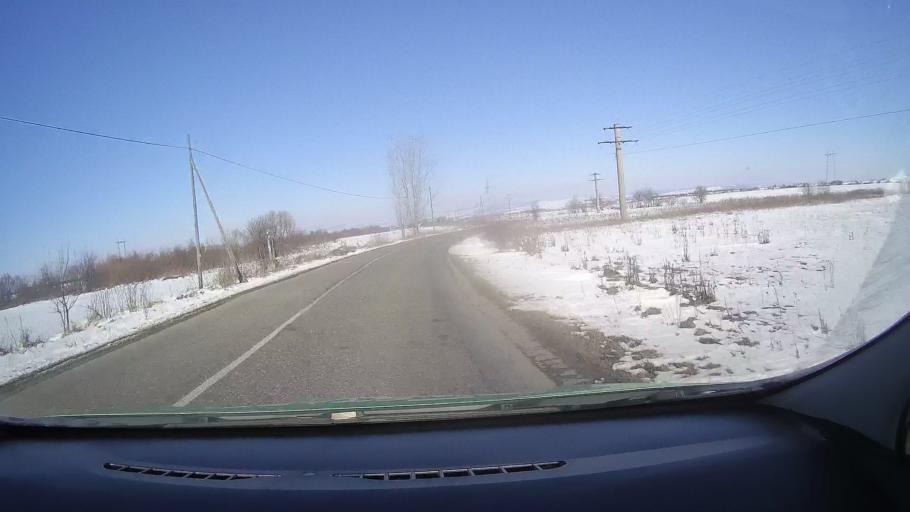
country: RO
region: Brasov
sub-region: Comuna Harseni
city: Harseni
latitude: 45.7720
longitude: 25.0012
